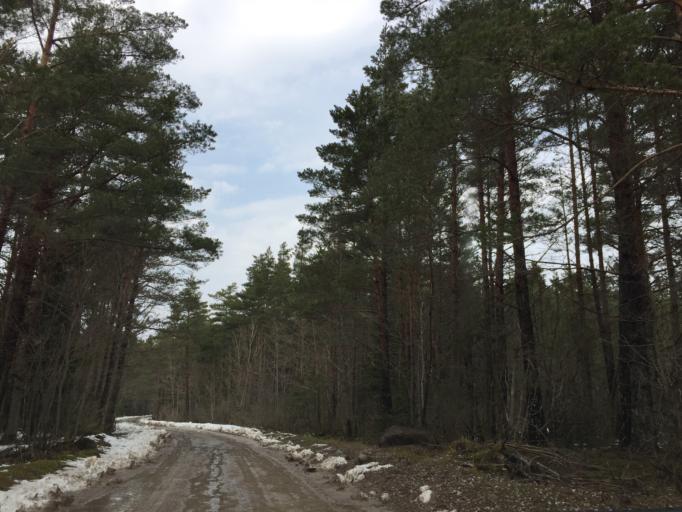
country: EE
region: Saare
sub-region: Kuressaare linn
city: Kuressaare
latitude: 58.4303
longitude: 22.1444
